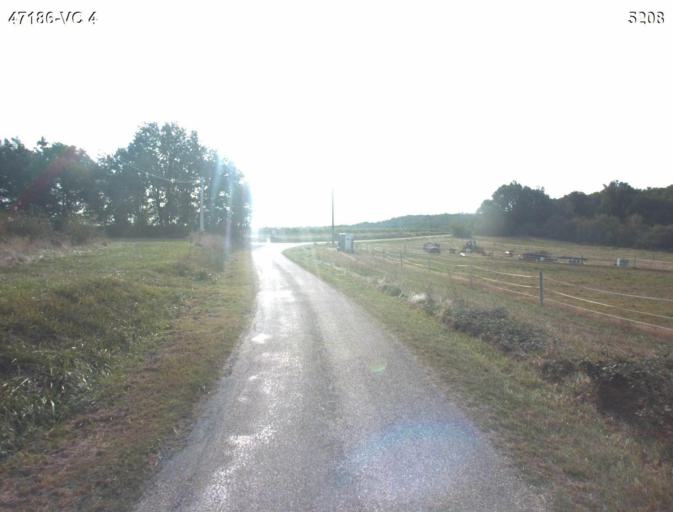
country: FR
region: Aquitaine
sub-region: Departement du Lot-et-Garonne
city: Sainte-Colombe-en-Bruilhois
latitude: 44.1892
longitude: 0.4580
